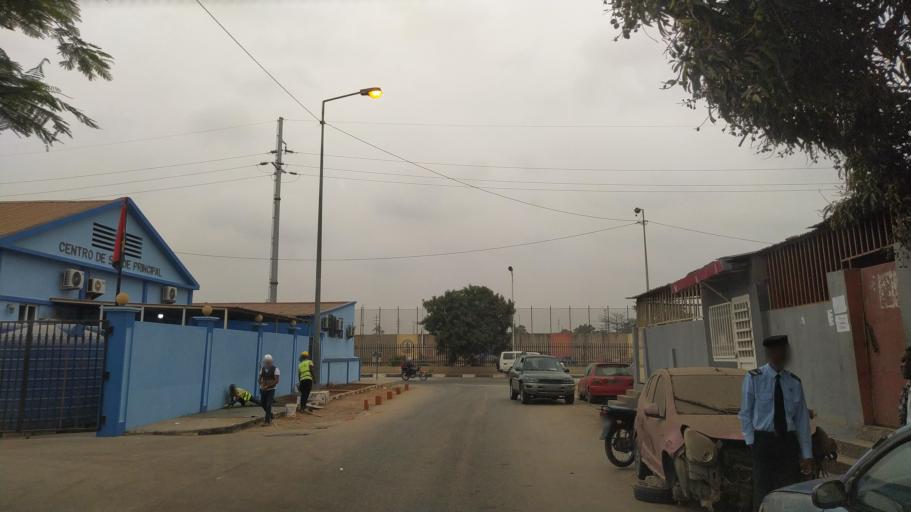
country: AO
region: Luanda
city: Luanda
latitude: -8.8360
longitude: 13.2544
